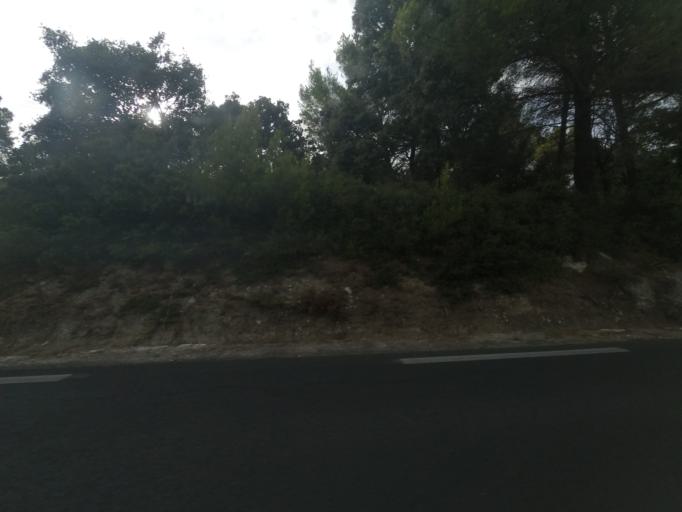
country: FR
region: Languedoc-Roussillon
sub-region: Departement de l'Herault
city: Restinclieres
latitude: 43.7106
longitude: 4.0281
